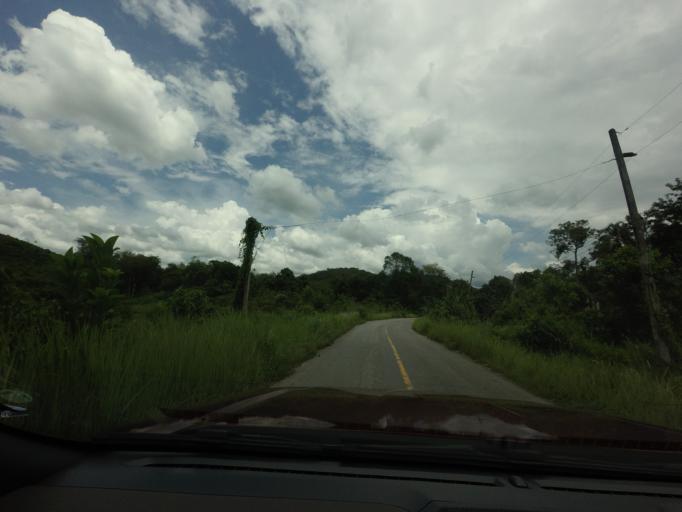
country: TH
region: Narathiwat
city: Chanae
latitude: 6.0415
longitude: 101.6923
